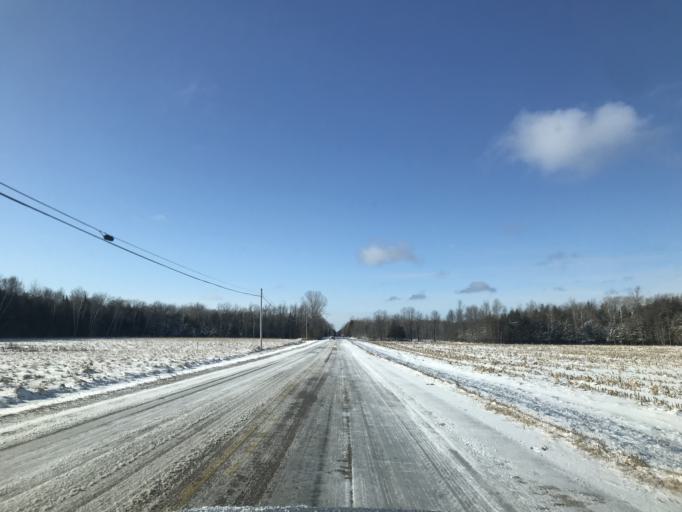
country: US
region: Wisconsin
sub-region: Door County
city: Sturgeon Bay
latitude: 44.8497
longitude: -87.4800
